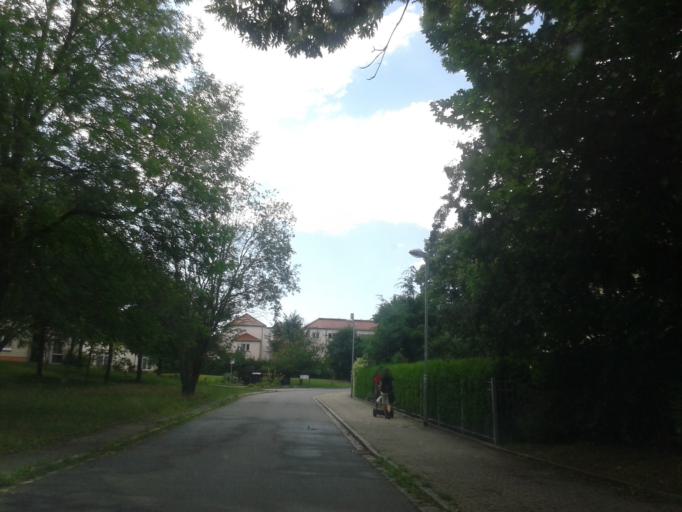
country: DE
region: Saxony
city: Radeberg
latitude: 51.1036
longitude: 13.9104
